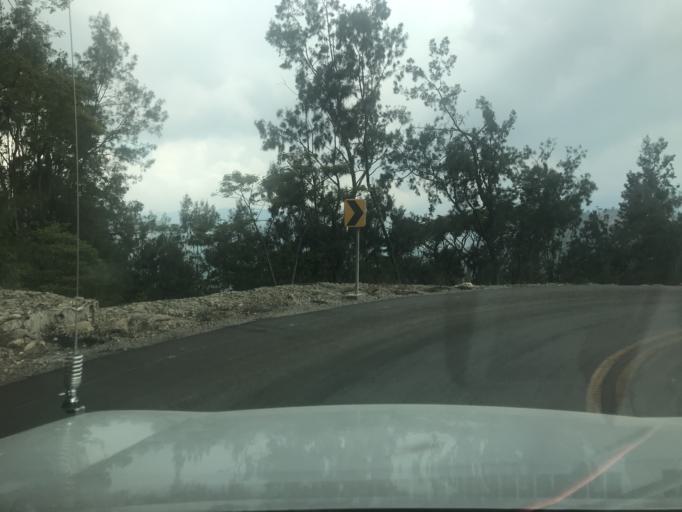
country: TL
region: Manufahi
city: Same
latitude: -8.8925
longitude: 125.5947
